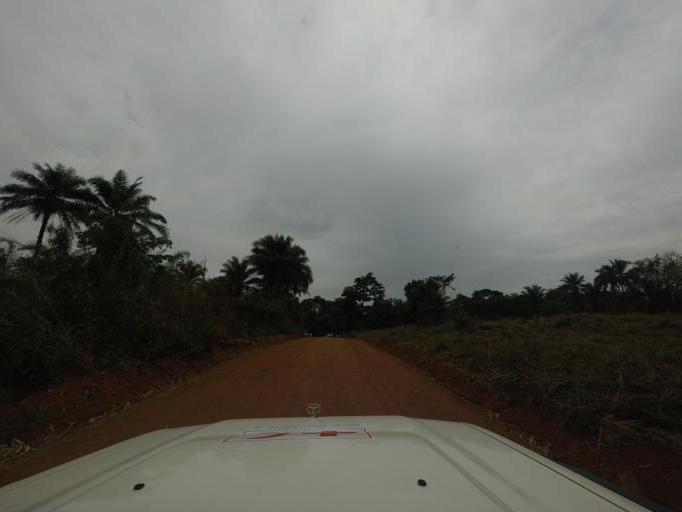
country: SL
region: Eastern Province
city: Buedu
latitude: 8.3426
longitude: -10.2056
